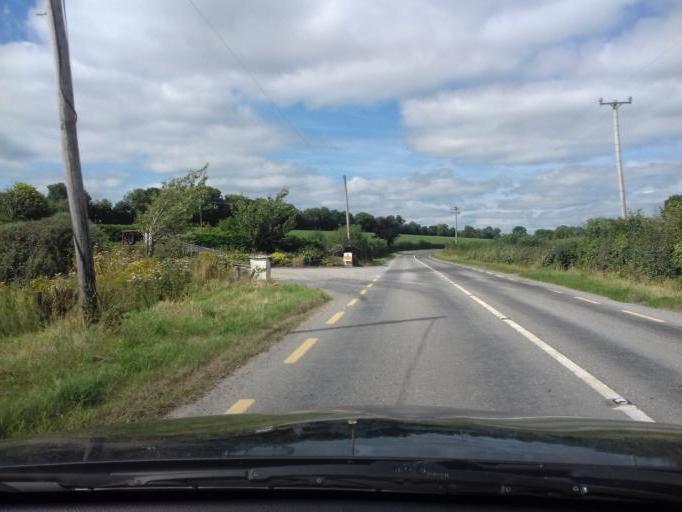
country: IE
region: Leinster
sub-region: Wicklow
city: Baltinglass
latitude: 53.0023
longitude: -6.6441
